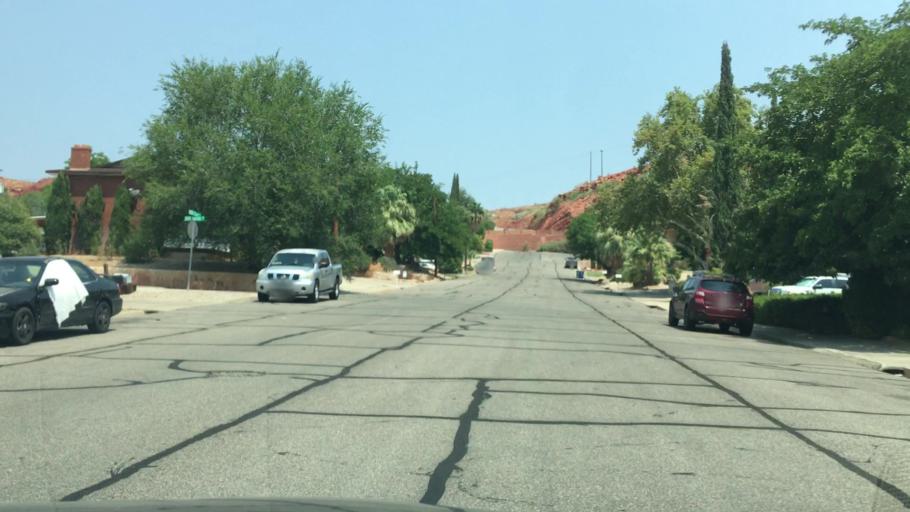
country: US
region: Utah
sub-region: Washington County
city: Saint George
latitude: 37.1130
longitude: -113.5812
